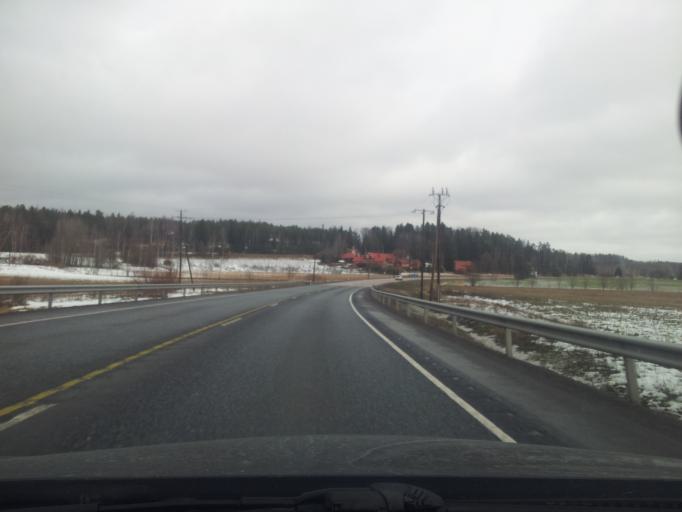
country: FI
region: Uusimaa
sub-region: Helsinki
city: Espoo
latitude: 60.1804
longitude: 24.5592
